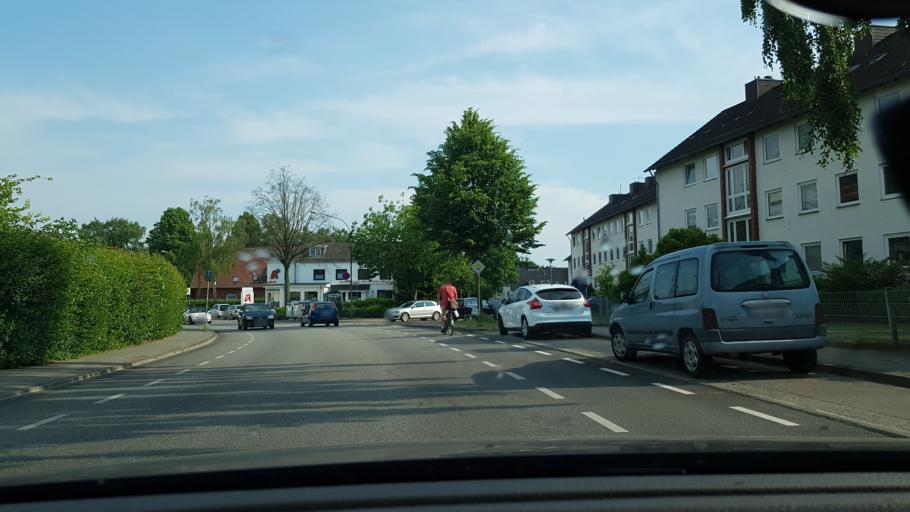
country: DE
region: Schleswig-Holstein
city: Luebeck
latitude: 53.8453
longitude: 10.6989
